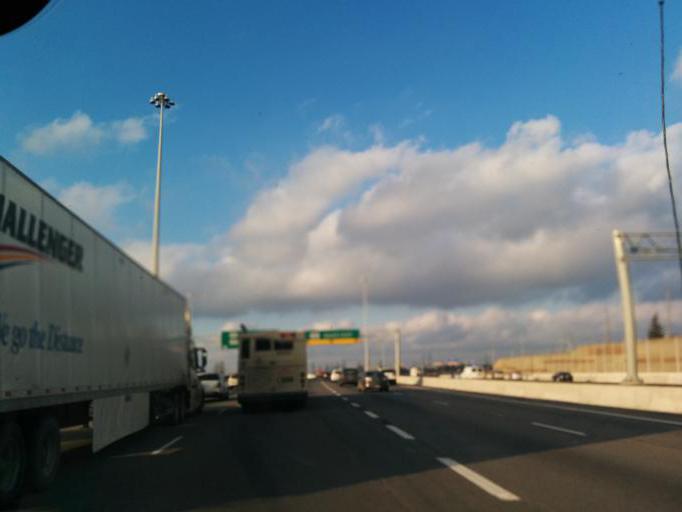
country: CA
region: Ontario
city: Etobicoke
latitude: 43.6672
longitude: -79.5730
